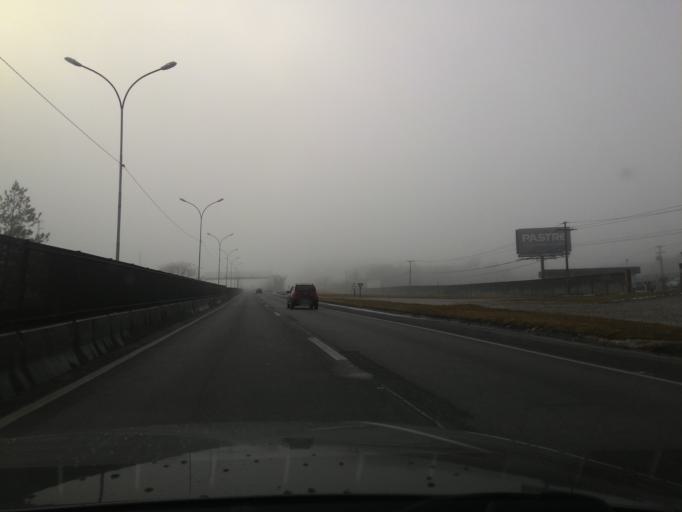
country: BR
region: Parana
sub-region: Quatro Barras
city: Quatro Barras
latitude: -25.3704
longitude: -49.1219
